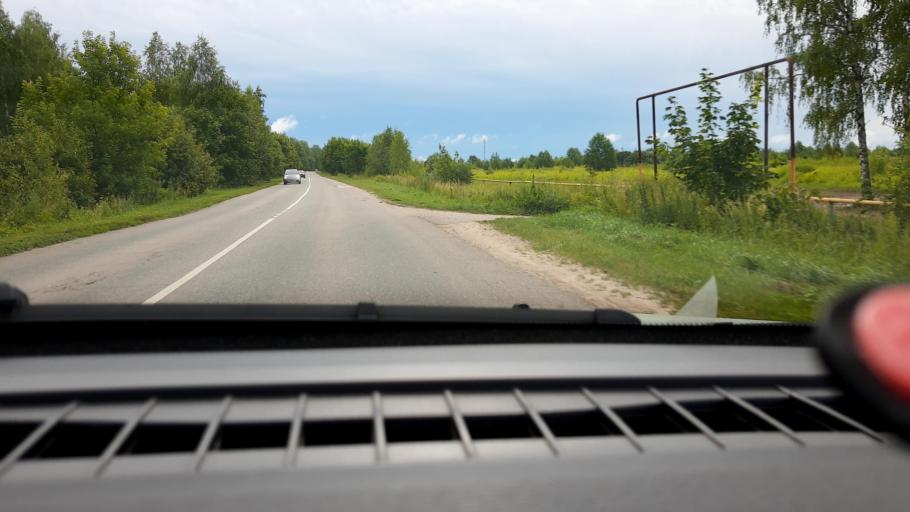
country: RU
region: Nizjnij Novgorod
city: Kstovo
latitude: 56.1485
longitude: 44.3099
